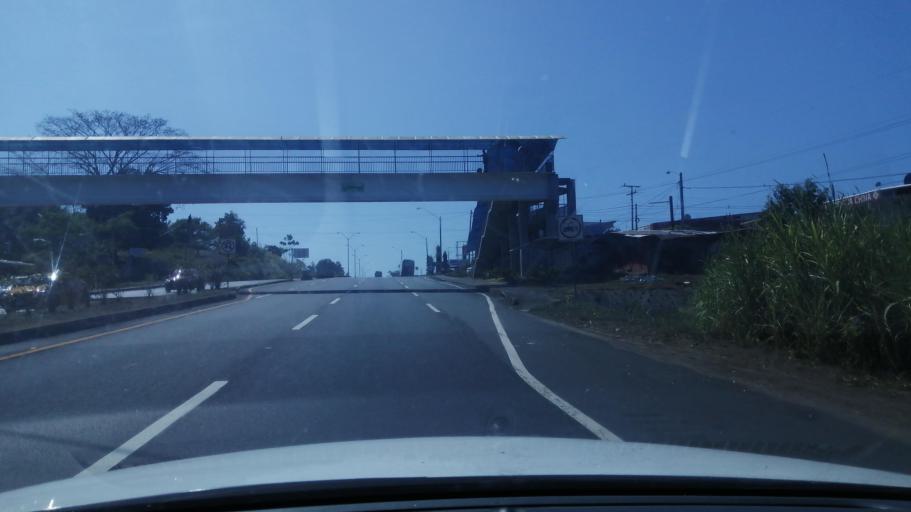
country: PA
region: Chiriqui
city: San Felix
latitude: 8.2775
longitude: -81.8709
